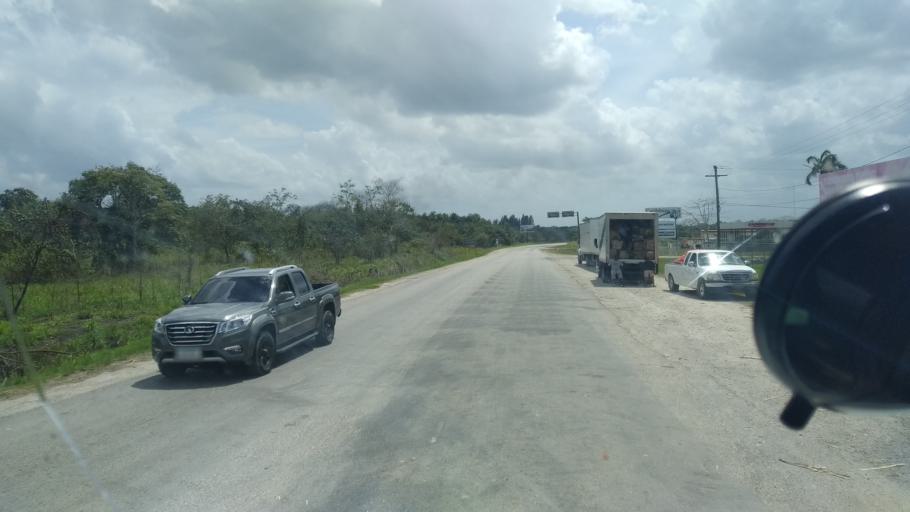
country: BZ
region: Orange Walk
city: Orange Walk
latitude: 18.0547
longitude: -88.5655
